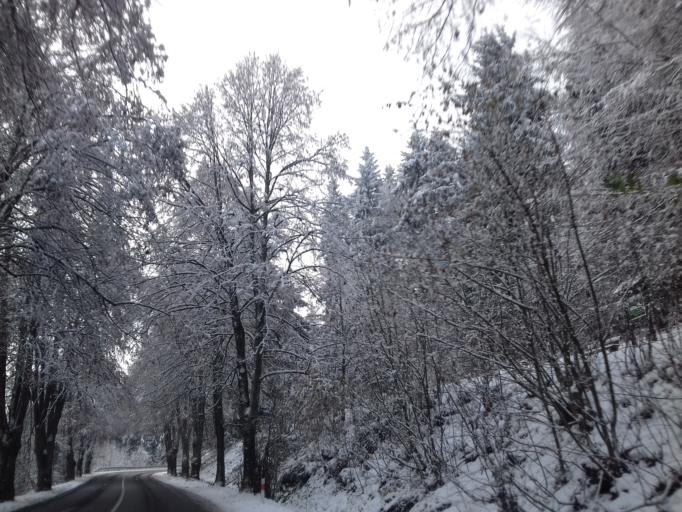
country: CZ
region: Plzensky
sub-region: Okres Domazlice
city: Klenci pod Cerchovem
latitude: 49.4132
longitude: 12.8041
